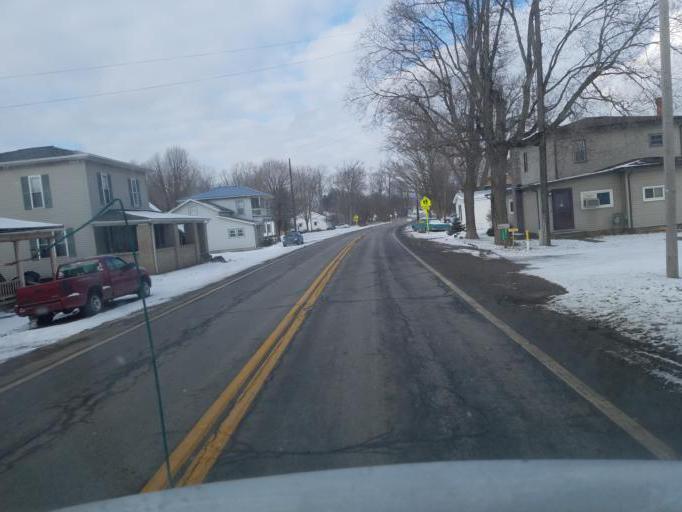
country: US
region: Ohio
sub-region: Holmes County
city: Millersburg
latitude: 40.4495
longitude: -81.9021
